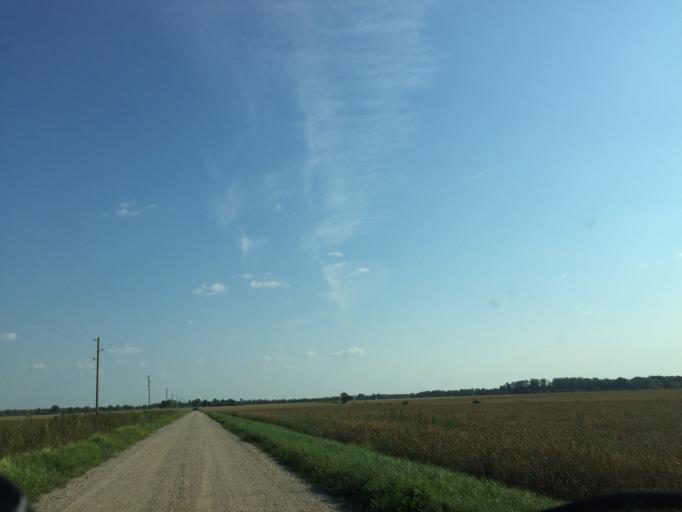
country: LV
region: Jelgava
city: Jelgava
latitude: 56.4653
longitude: 23.6802
